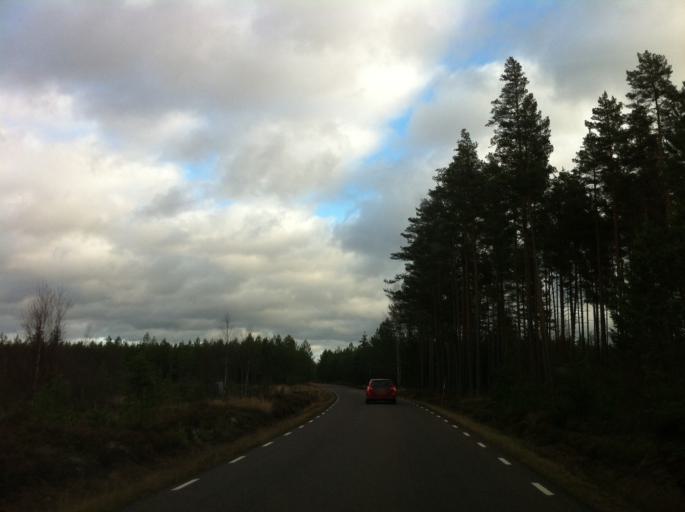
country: SE
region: Kalmar
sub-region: Hultsfreds Kommun
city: Hultsfred
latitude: 57.5310
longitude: 15.7398
